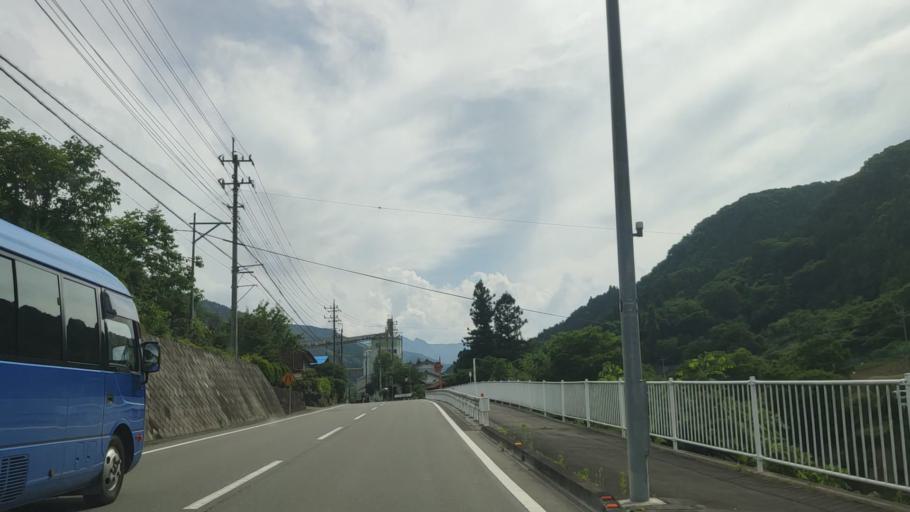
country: JP
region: Gunma
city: Tomioka
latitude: 36.1885
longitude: 138.7501
